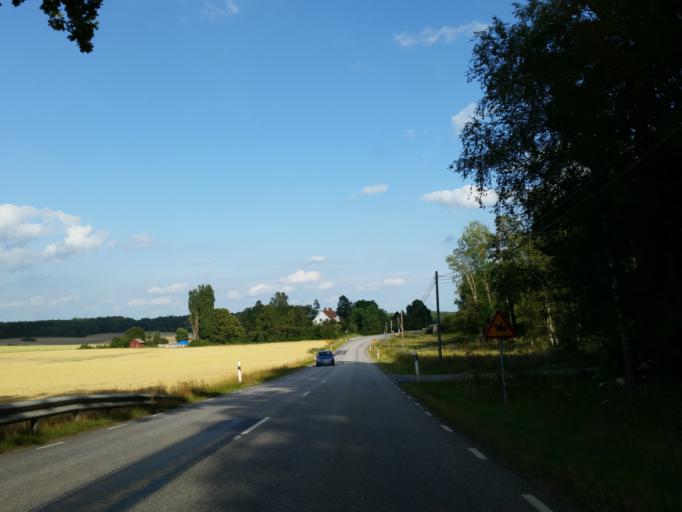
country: SE
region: Stockholm
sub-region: Nykvarns Kommun
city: Nykvarn
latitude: 59.2057
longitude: 17.3941
